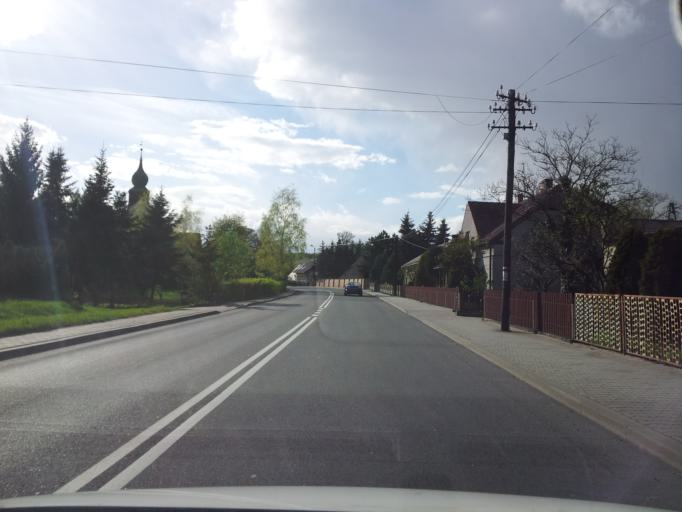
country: PL
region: Lubusz
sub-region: Powiat zielonogorski
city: Czerwiensk
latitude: 51.9867
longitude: 15.3143
